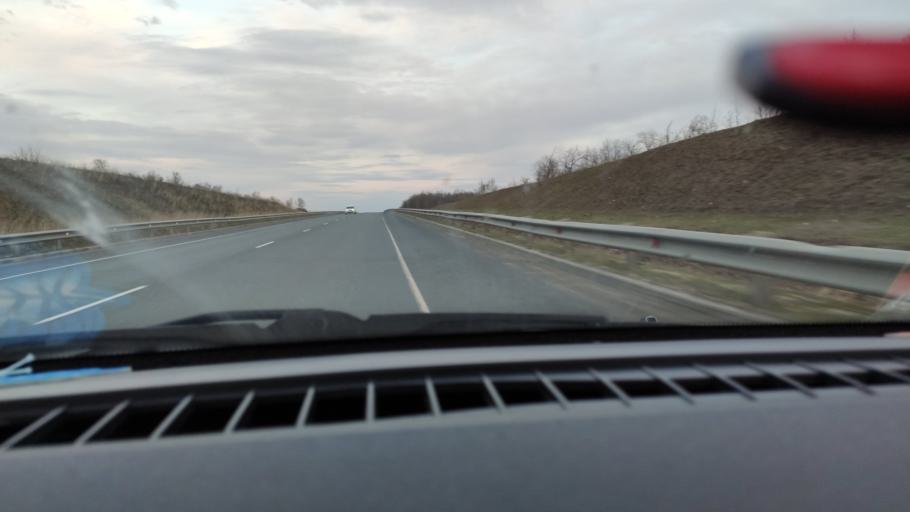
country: RU
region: Saratov
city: Yelshanka
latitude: 51.8212
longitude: 46.3403
